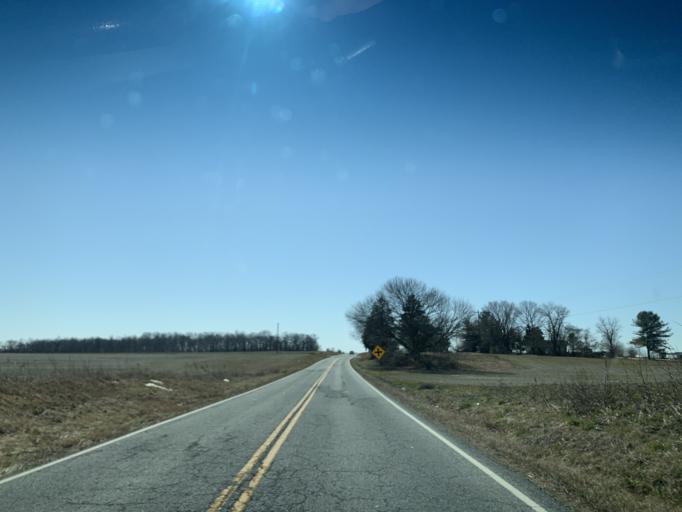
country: US
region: Maryland
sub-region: Cecil County
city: Charlestown
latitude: 39.4389
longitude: -75.9071
